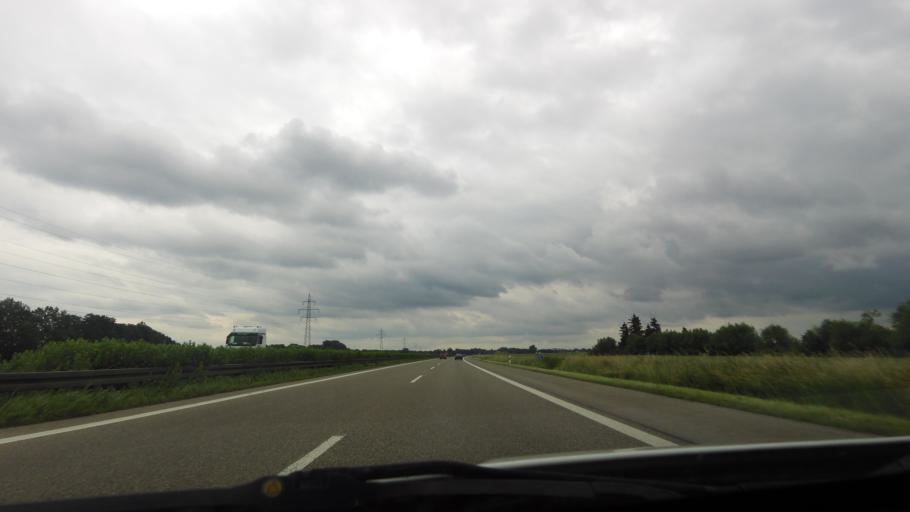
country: DE
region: Baden-Wuerttemberg
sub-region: Tuebingen Region
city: Dettingen an der Iller
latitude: 48.0994
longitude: 10.1323
